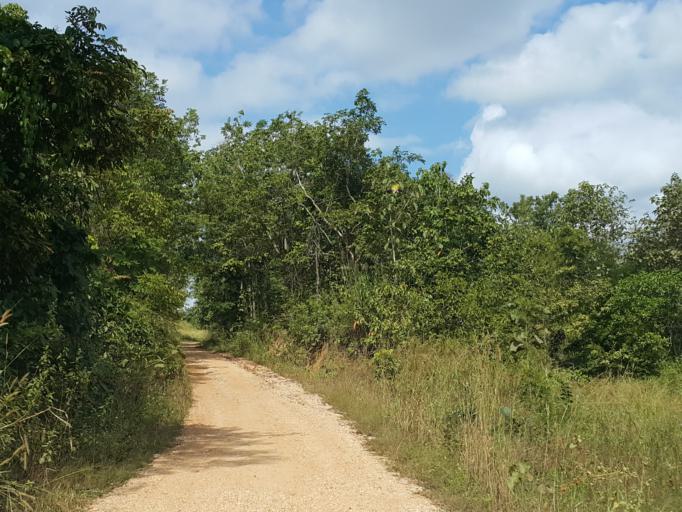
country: TH
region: Lampang
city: Hang Chat
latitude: 18.4813
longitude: 99.4160
